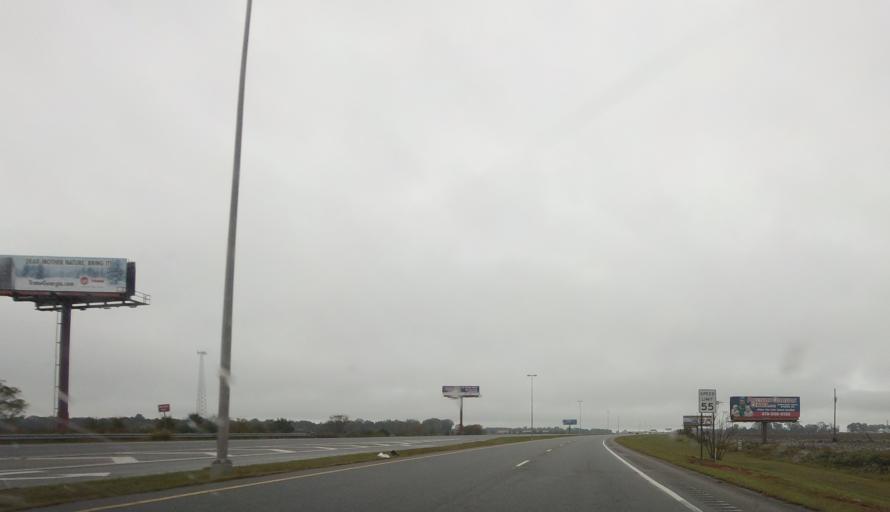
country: US
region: Georgia
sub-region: Houston County
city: Centerville
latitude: 32.5862
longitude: -83.7384
